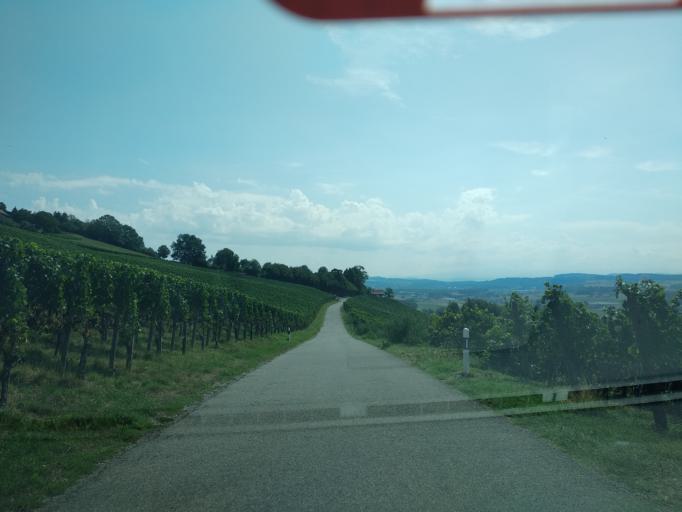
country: CH
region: Thurgau
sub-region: Frauenfeld District
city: Huttwilen
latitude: 47.5859
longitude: 8.8229
